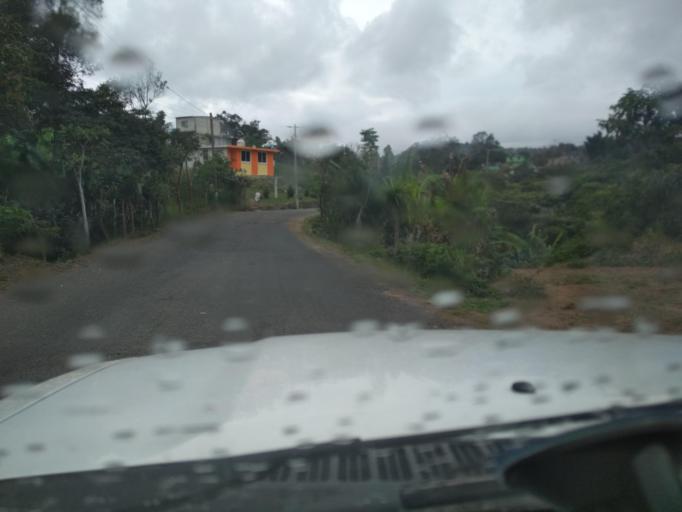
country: MX
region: Veracruz
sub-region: Emiliano Zapata
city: Dos Rios
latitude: 19.5342
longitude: -96.8128
